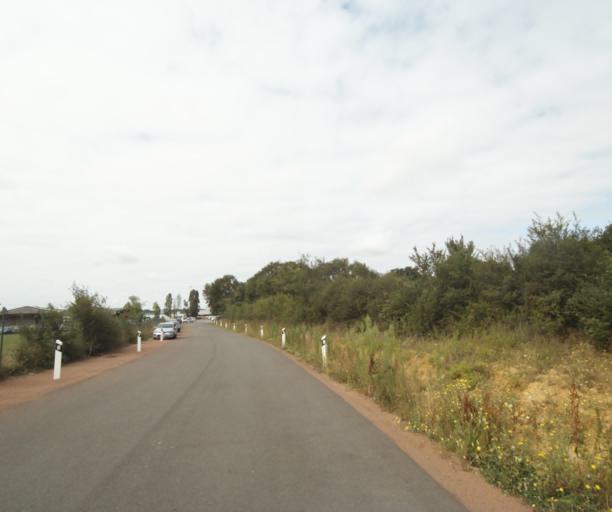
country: FR
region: Pays de la Loire
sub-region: Departement de la Sarthe
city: Solesmes
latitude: 47.8285
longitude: -0.3056
